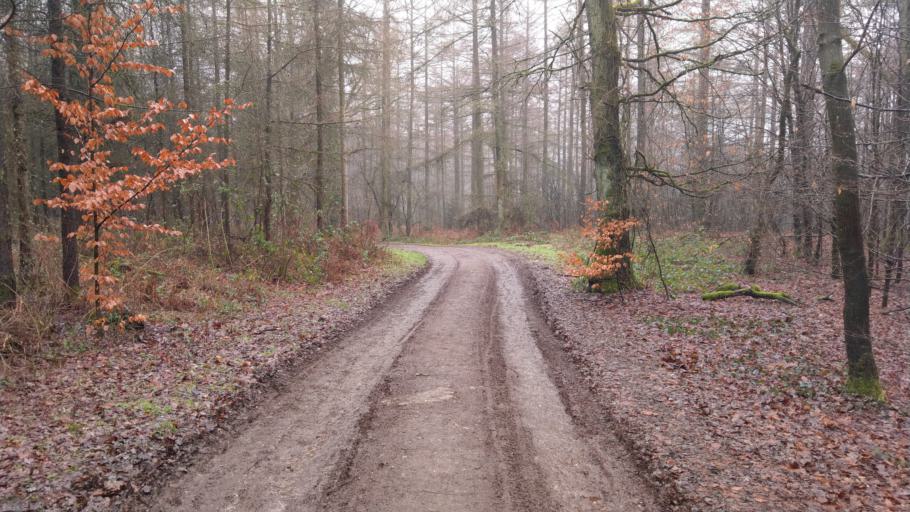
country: BE
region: Wallonia
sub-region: Province de Liege
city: La Calamine
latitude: 50.7322
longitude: 6.0252
